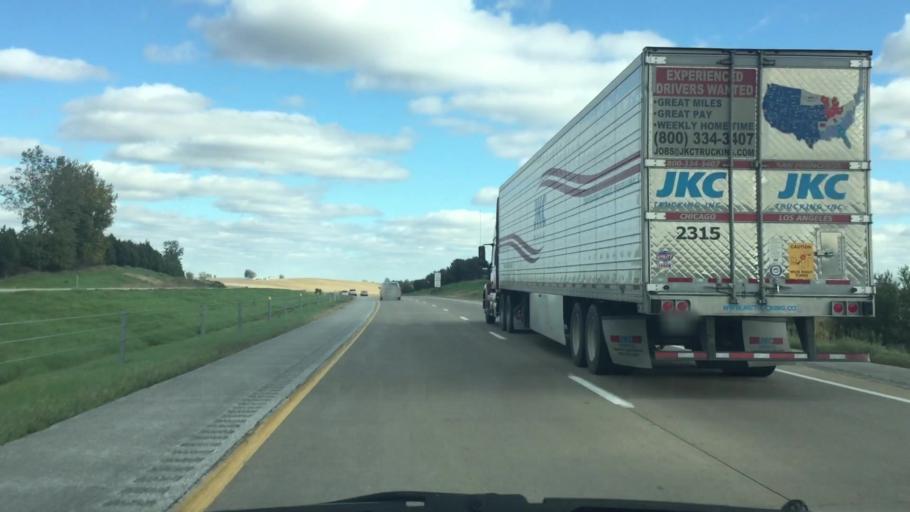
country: US
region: Iowa
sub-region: Muscatine County
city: Wilton
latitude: 41.6340
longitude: -91.0265
